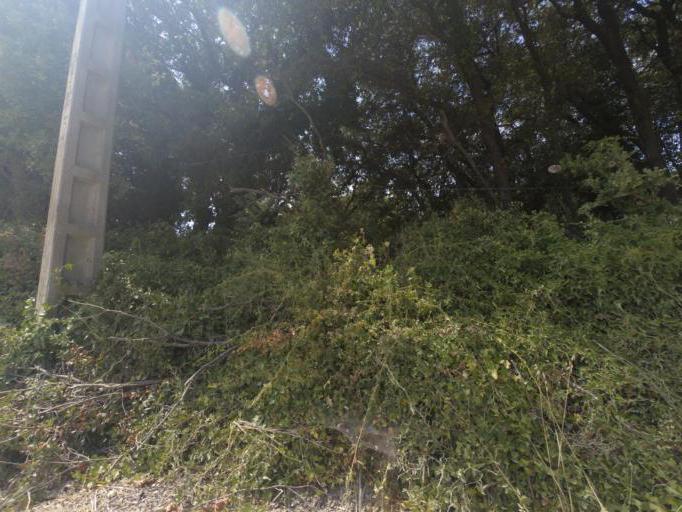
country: FR
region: Languedoc-Roussillon
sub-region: Departement du Gard
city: Aubais
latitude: 43.7647
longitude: 4.1179
